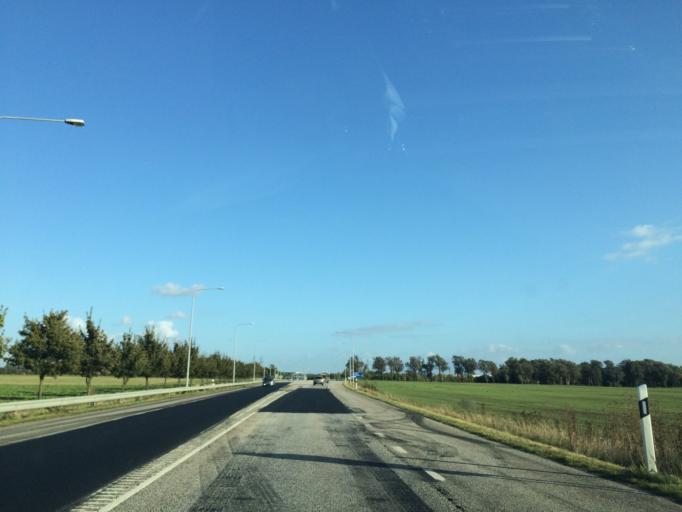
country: SE
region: Skane
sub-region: Staffanstorps Kommun
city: Hjaerup
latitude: 55.7208
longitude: 13.1425
